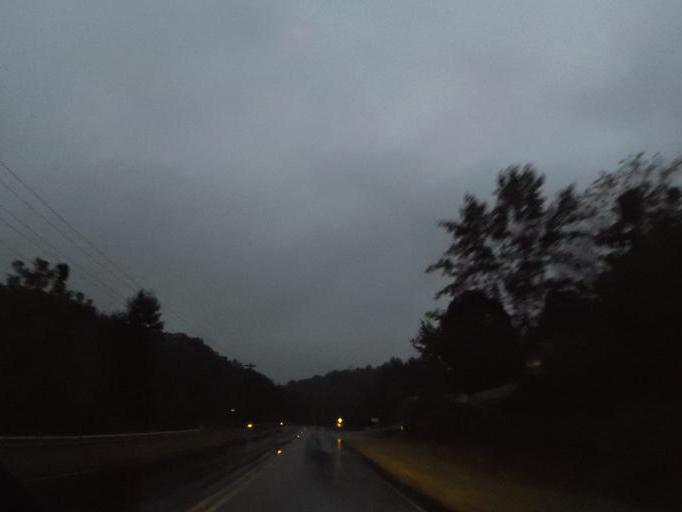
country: US
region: North Carolina
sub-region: Alleghany County
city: Sparta
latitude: 36.5401
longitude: -81.1569
